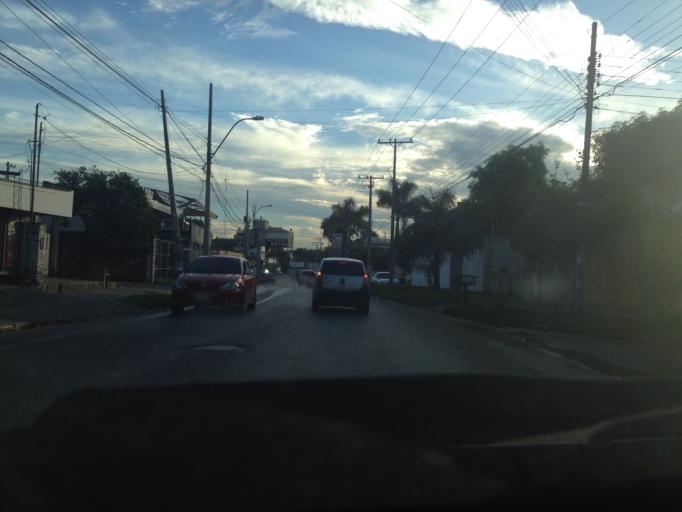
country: PY
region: Central
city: Lambare
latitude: -25.3326
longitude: -57.5885
